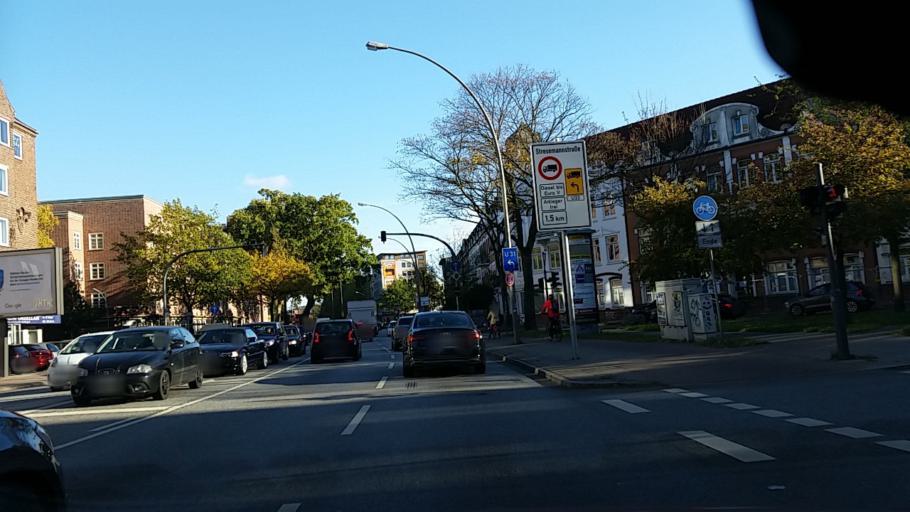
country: DE
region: Hamburg
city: Altona
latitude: 53.5644
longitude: 9.9165
